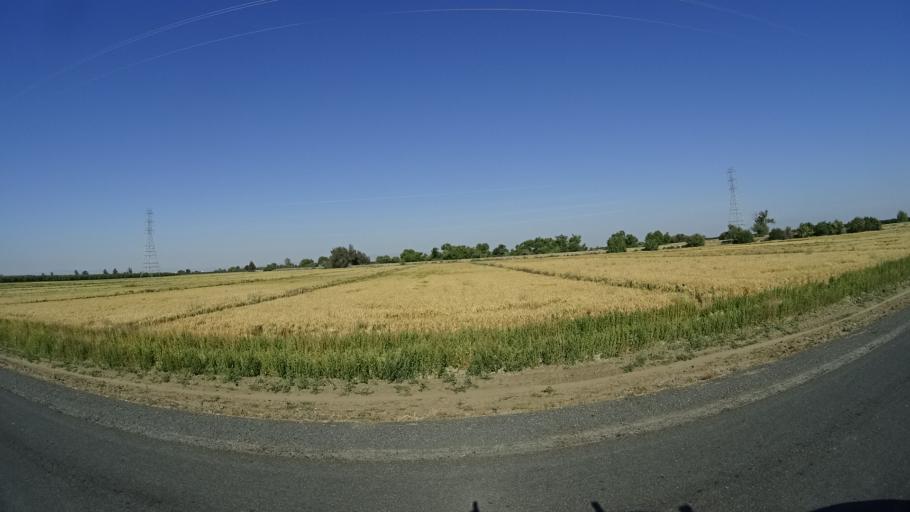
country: US
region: California
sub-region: Fresno County
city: Riverdale
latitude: 36.3717
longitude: -119.8871
